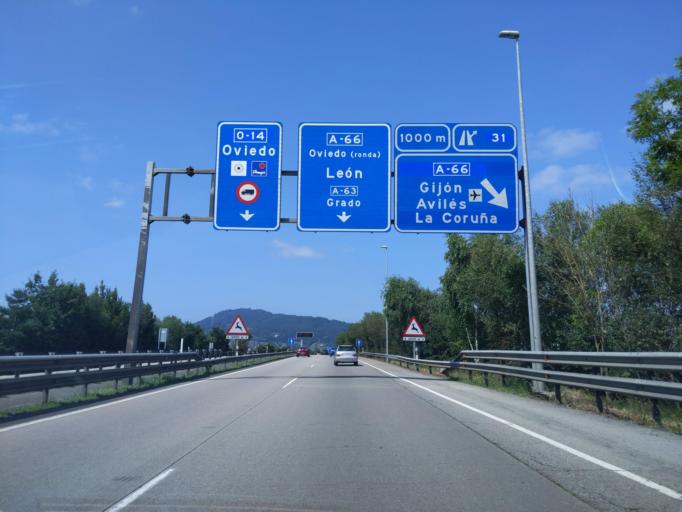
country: ES
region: Asturias
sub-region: Province of Asturias
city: Lugones
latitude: 43.3926
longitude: -5.7861
